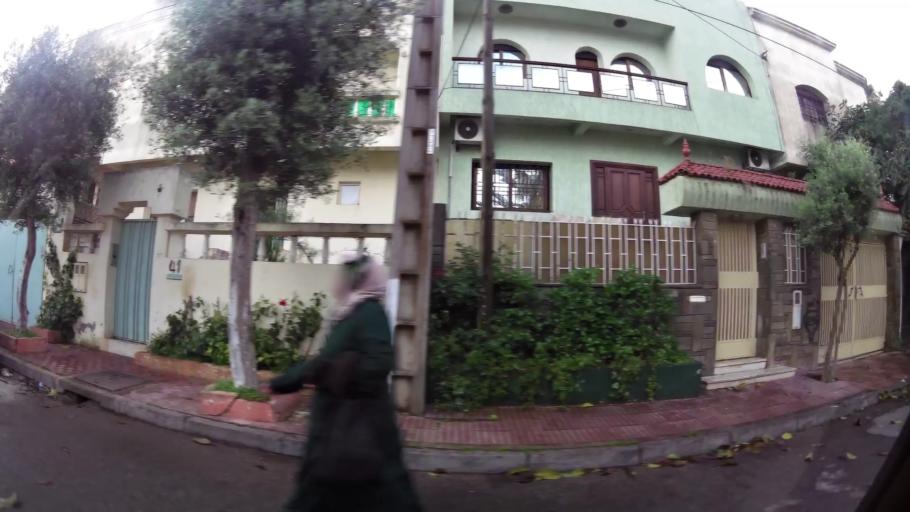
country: MA
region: Grand Casablanca
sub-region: Casablanca
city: Casablanca
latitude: 33.5600
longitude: -7.6766
